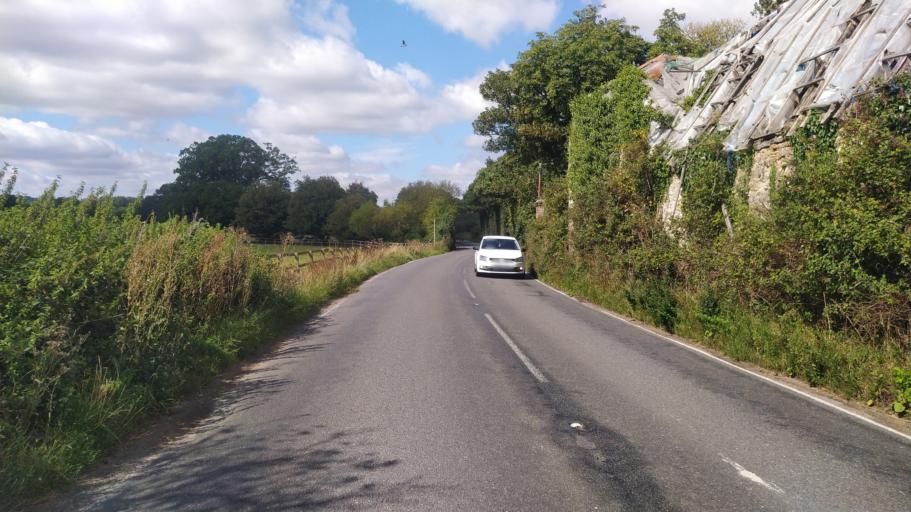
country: GB
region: England
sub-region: Hampshire
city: Kingsley
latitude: 51.1338
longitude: -0.8916
